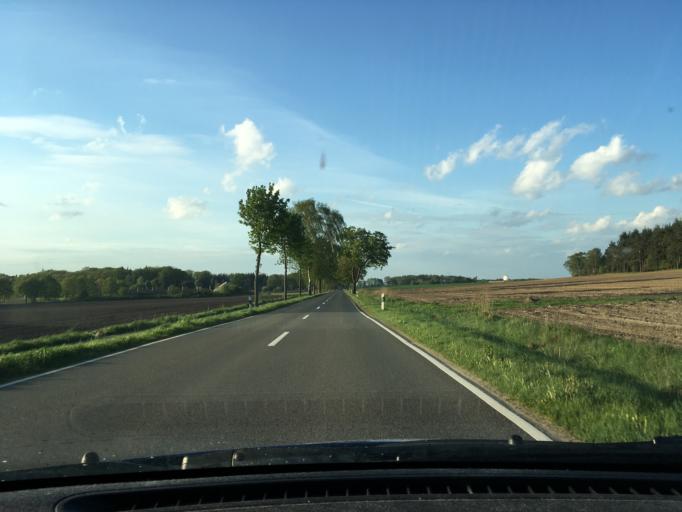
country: DE
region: Lower Saxony
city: Wietzendorf
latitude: 52.8845
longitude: 9.9827
